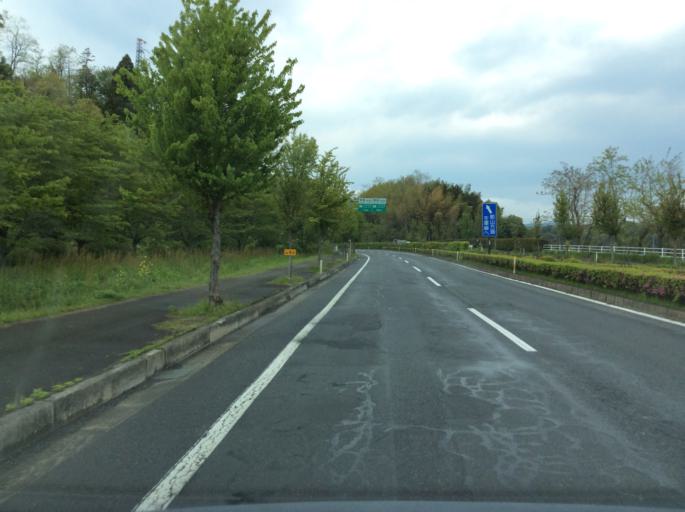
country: JP
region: Fukushima
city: Iwaki
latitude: 37.0655
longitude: 140.8488
